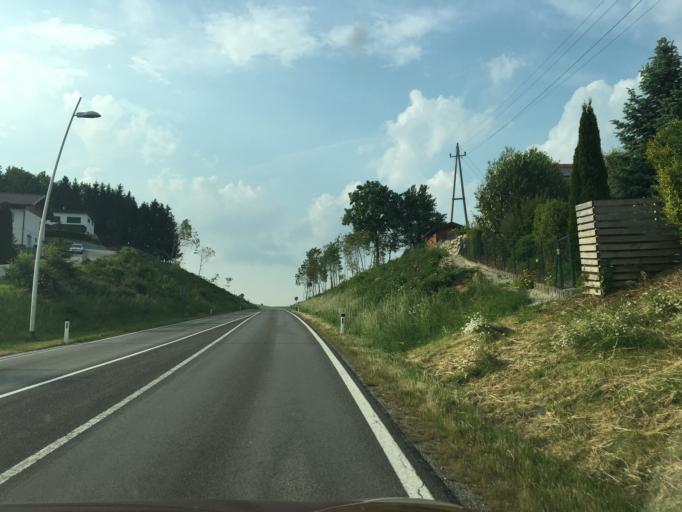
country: AT
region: Upper Austria
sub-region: Politischer Bezirk Ried im Innkreis
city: Ried im Innkreis
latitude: 48.1833
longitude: 13.5764
